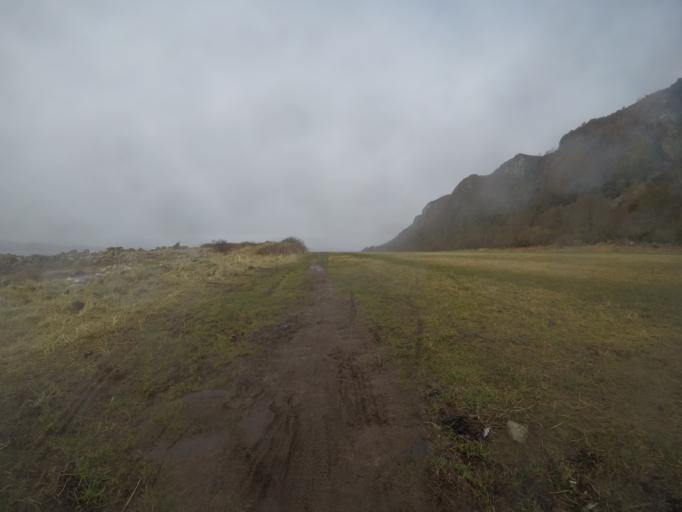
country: GB
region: Scotland
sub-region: North Ayrshire
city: Millport
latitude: 55.7063
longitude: -4.9041
